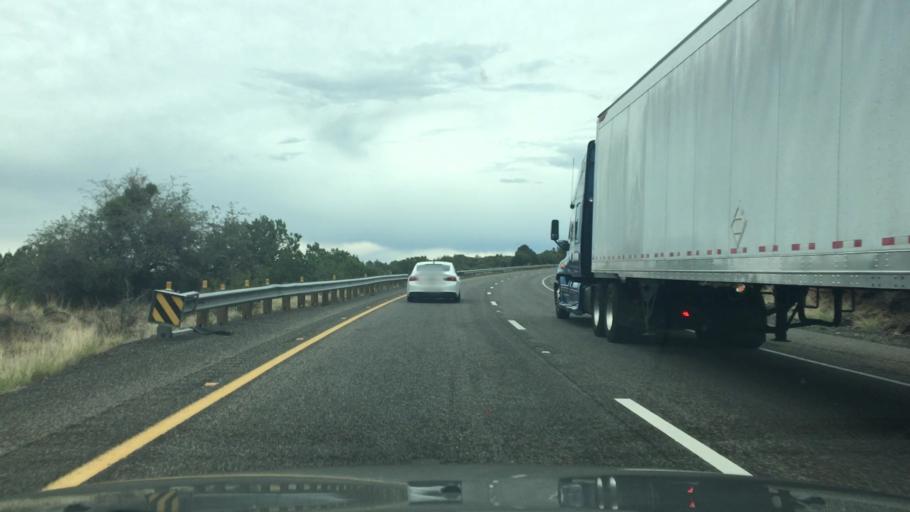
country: US
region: Arizona
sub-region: Yavapai County
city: Village of Oak Creek (Big Park)
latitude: 34.7724
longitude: -111.6375
